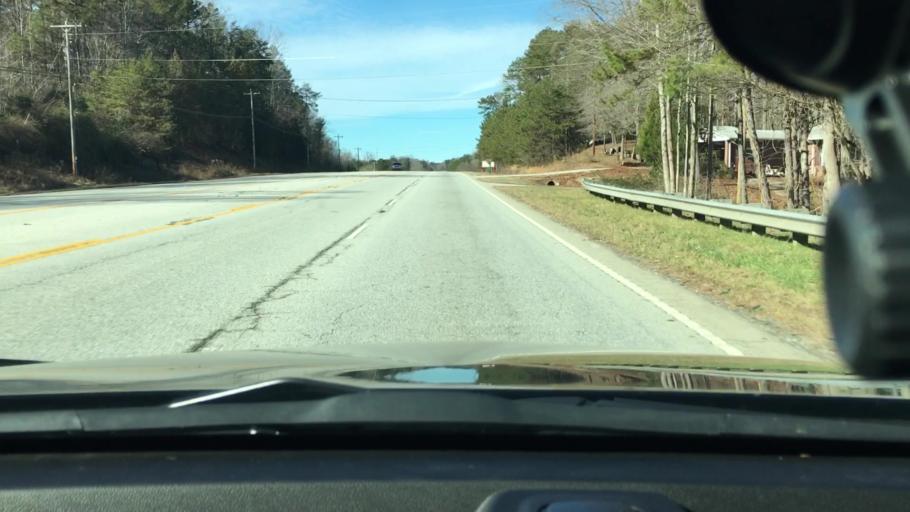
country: US
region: South Carolina
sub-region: Spartanburg County
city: Pacolet
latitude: 34.9125
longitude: -81.8071
